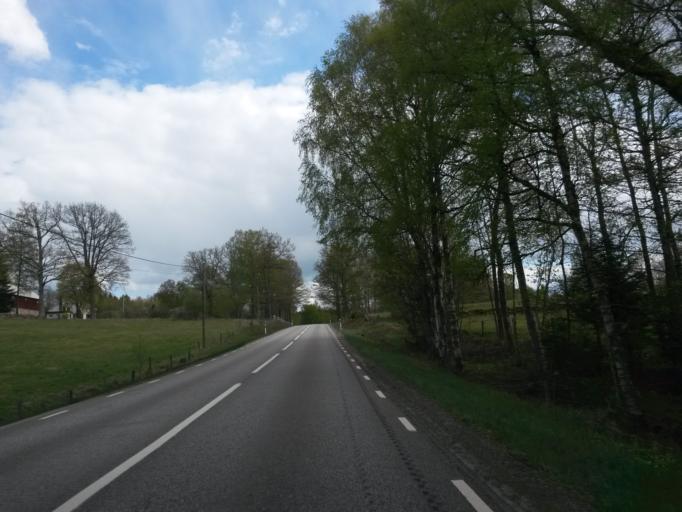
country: SE
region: Vaestra Goetaland
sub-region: Vargarda Kommun
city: Vargarda
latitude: 57.9241
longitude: 12.8639
